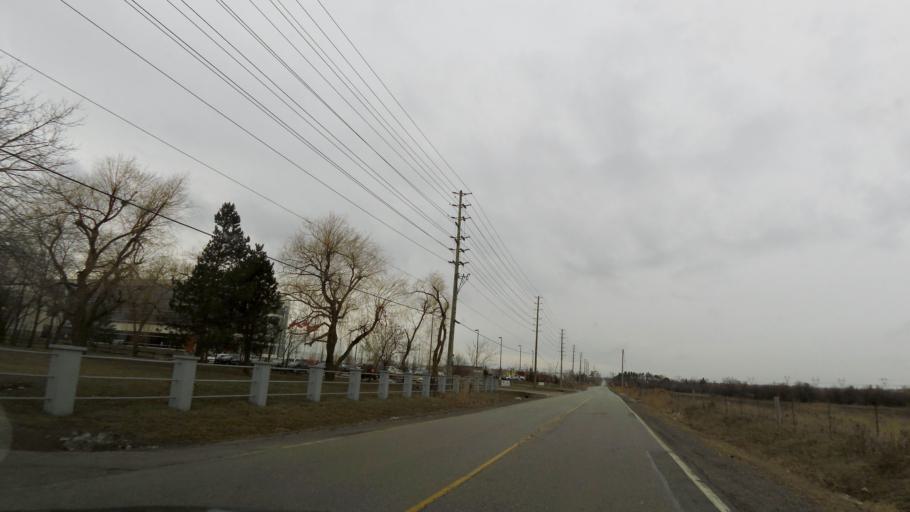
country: CA
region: Ontario
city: Brampton
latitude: 43.7914
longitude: -79.6522
